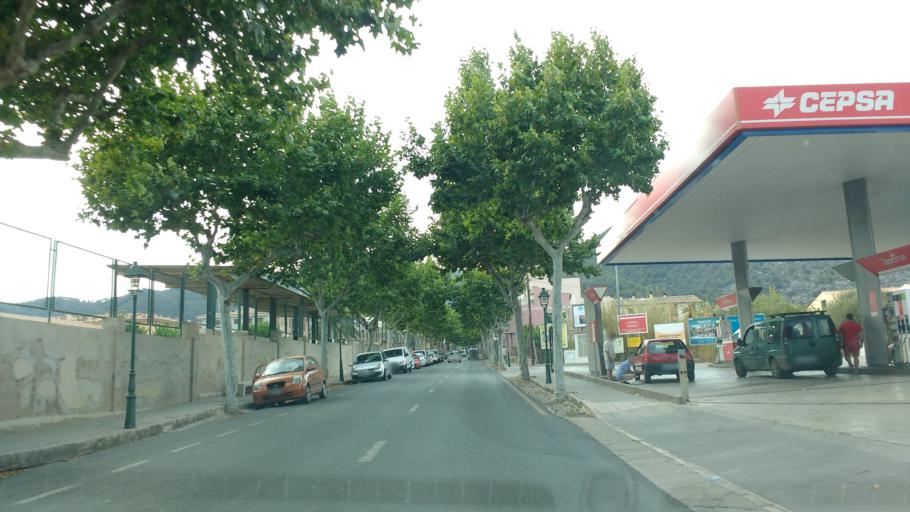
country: ES
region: Balearic Islands
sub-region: Illes Balears
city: Alaro
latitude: 39.7019
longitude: 2.7950
